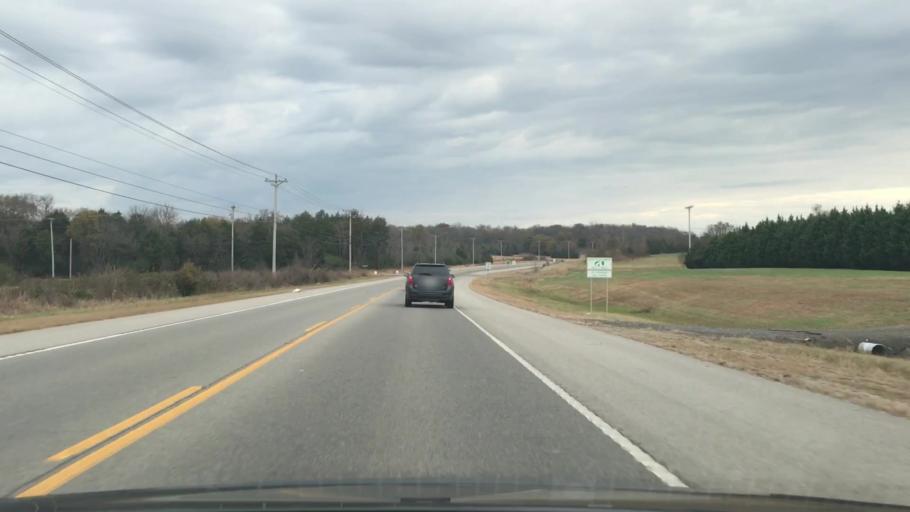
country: US
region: Tennessee
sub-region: Wilson County
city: Lebanon
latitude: 36.2636
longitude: -86.2397
